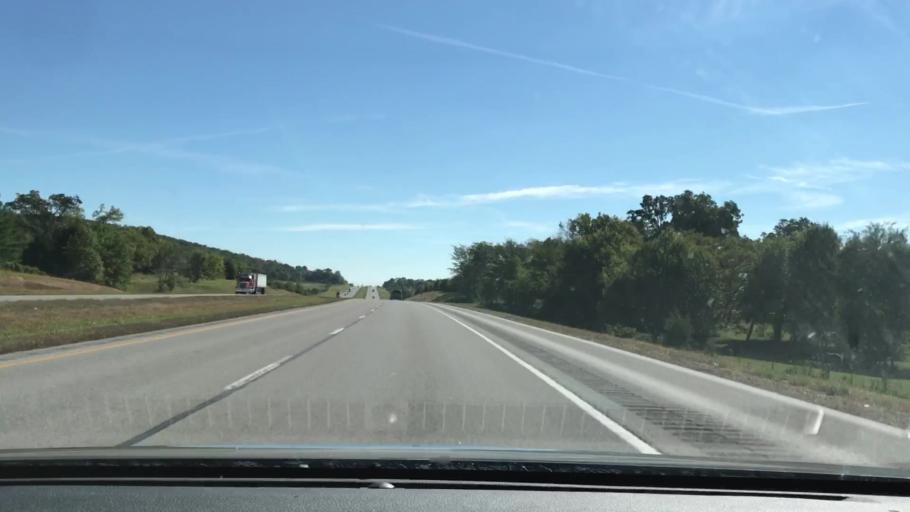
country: US
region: Kentucky
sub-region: Todd County
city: Elkton
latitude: 36.8262
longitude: -87.2182
